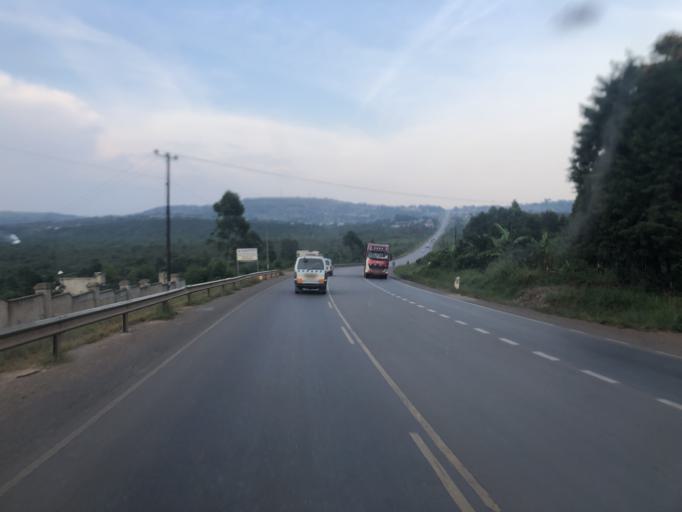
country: UG
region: Central Region
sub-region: Mpigi District
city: Mpigi
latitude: 0.2410
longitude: 32.3511
